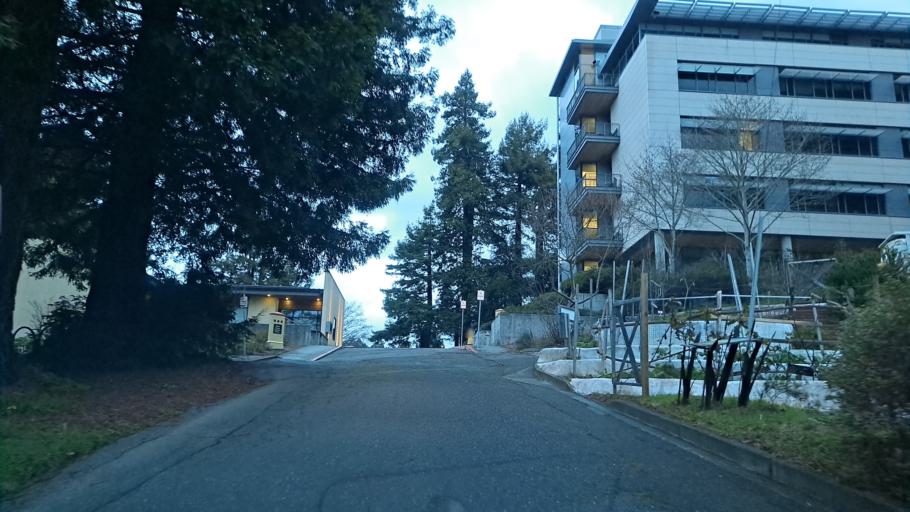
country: US
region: California
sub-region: Humboldt County
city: Arcata
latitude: 40.8725
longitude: -124.0778
